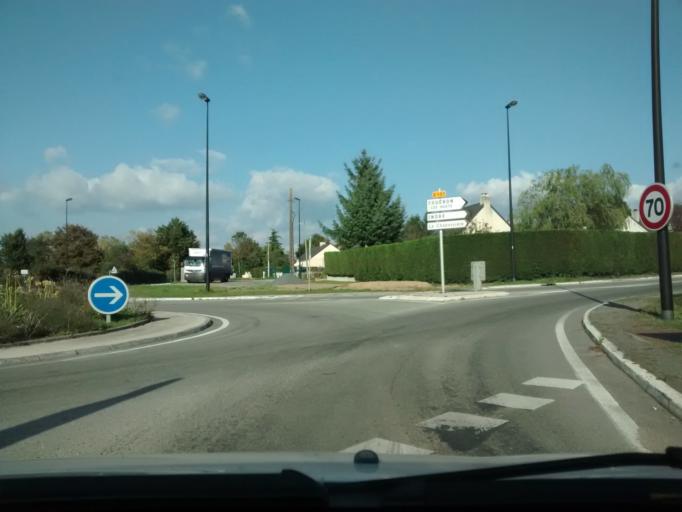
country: FR
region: Pays de la Loire
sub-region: Departement de la Loire-Atlantique
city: Sautron
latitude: 47.2446
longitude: -1.6912
